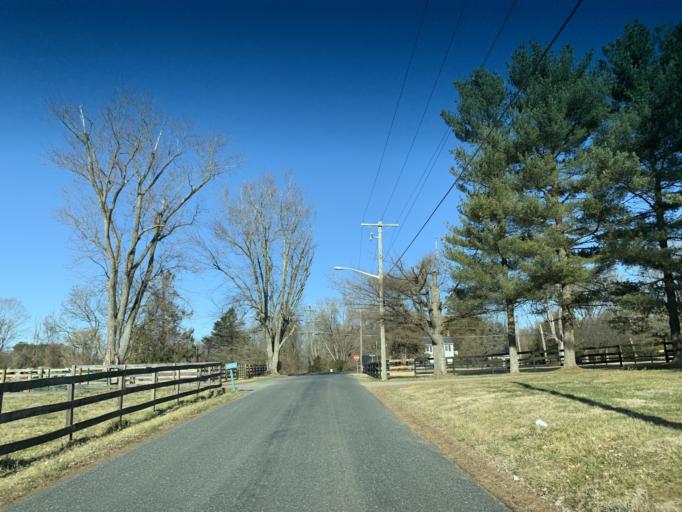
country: US
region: Maryland
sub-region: Harford County
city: South Bel Air
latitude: 39.6258
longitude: -76.2750
